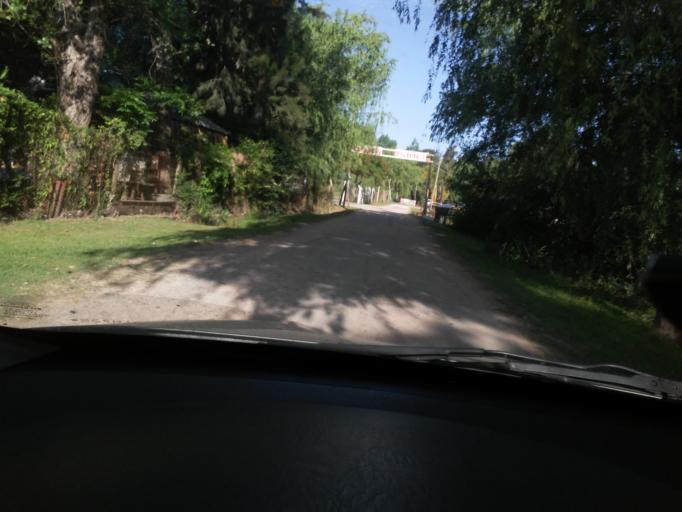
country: AR
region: Buenos Aires
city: Belen de Escobar
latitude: -34.2499
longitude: -58.7189
